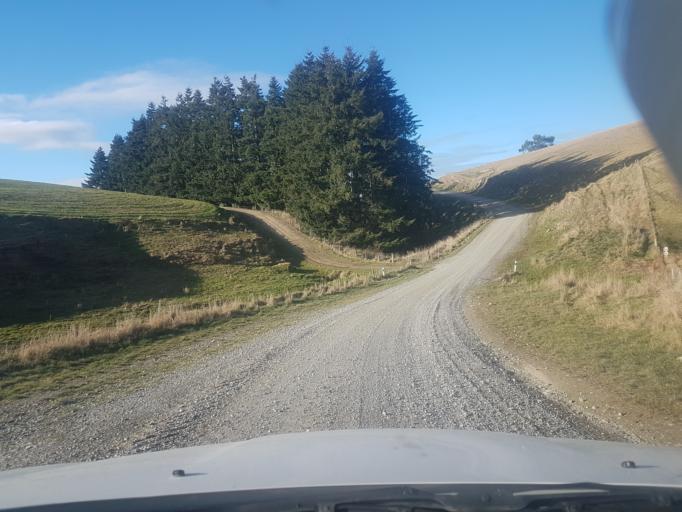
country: NZ
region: Canterbury
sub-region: Timaru District
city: Pleasant Point
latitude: -44.1669
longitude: 170.9118
